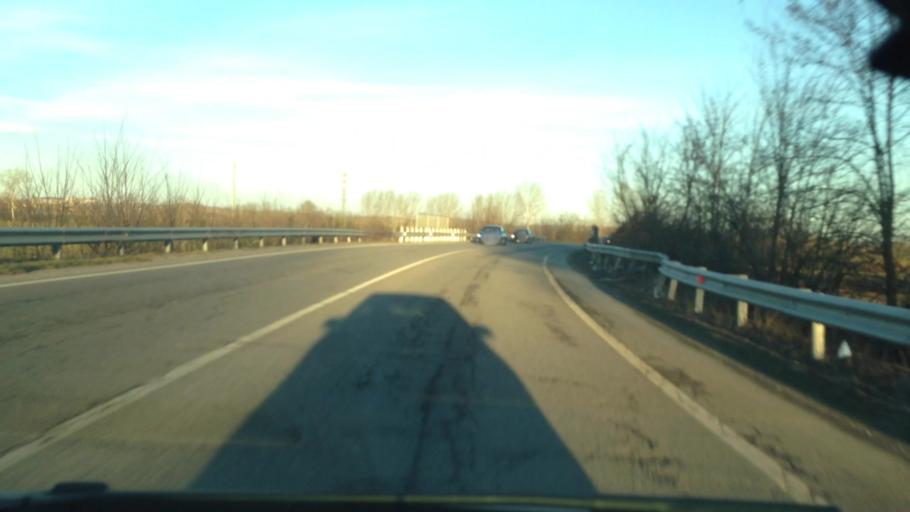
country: IT
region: Piedmont
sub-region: Provincia di Alessandria
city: Solero
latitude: 44.9215
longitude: 8.5016
